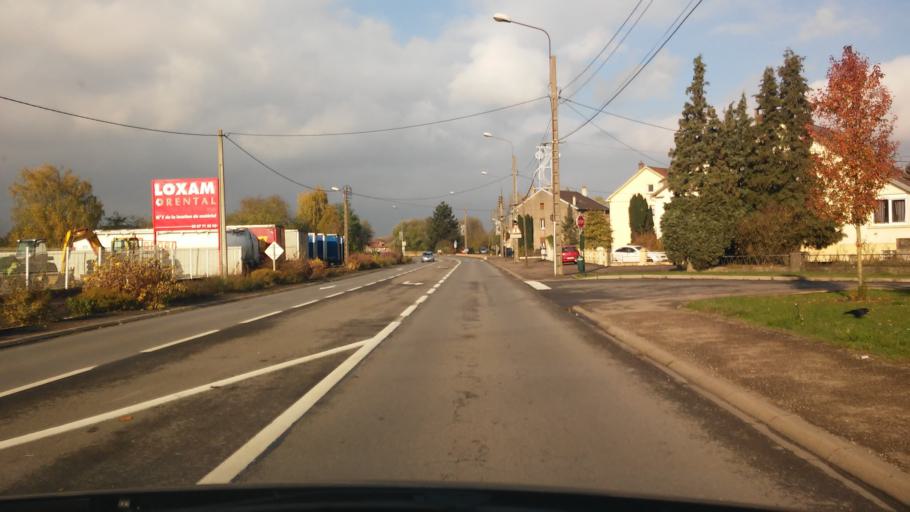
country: FR
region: Lorraine
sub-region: Departement de la Moselle
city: Richemont
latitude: 49.2756
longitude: 6.1707
